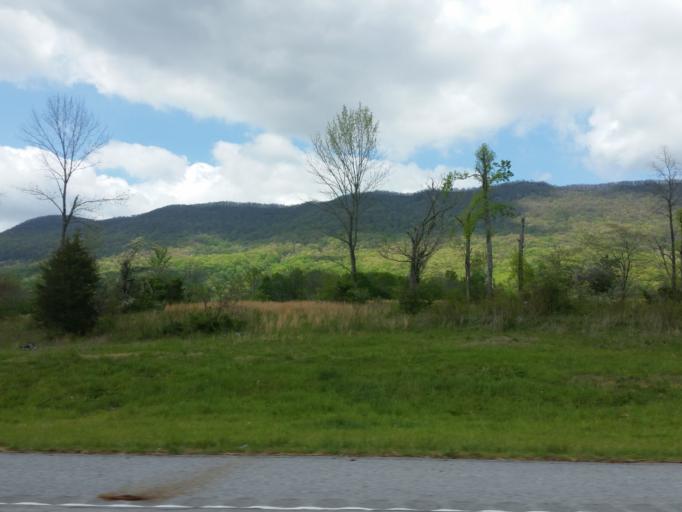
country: US
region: Tennessee
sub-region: Campbell County
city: Fincastle
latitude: 36.4494
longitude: -83.9282
